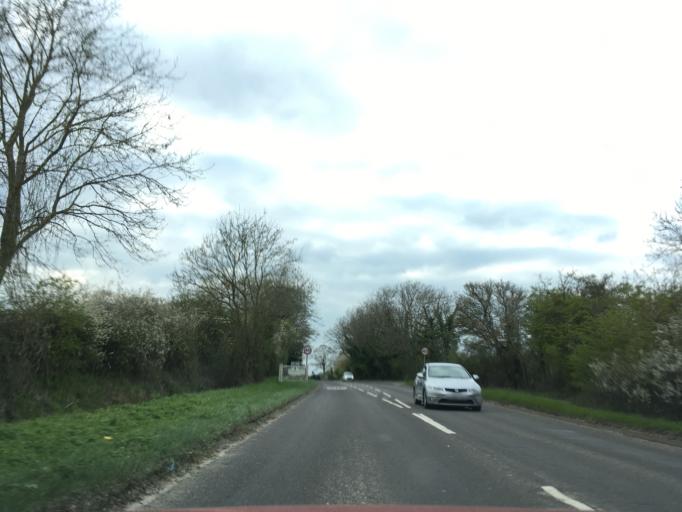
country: GB
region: England
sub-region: Oxfordshire
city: Witney
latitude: 51.7963
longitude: -1.5405
